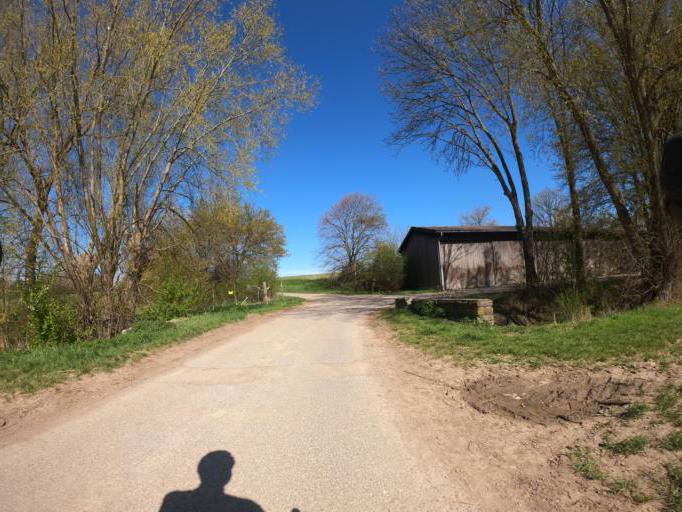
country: DE
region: Baden-Wuerttemberg
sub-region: Karlsruhe Region
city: Wiernsheim
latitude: 48.9061
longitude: 8.8569
